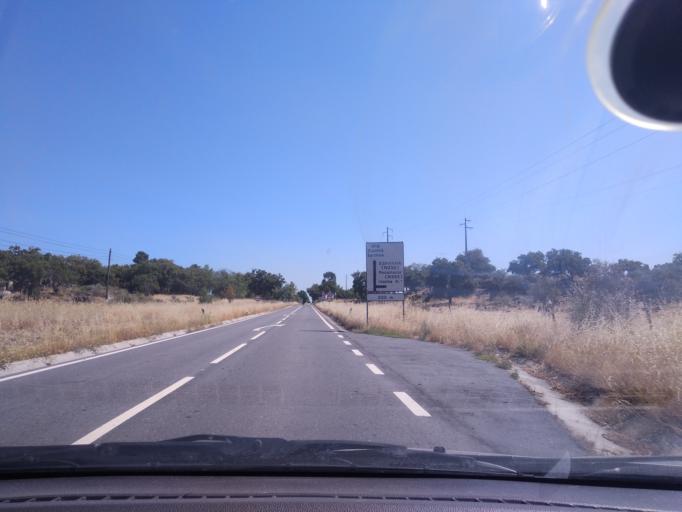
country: PT
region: Guarda
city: Alcains
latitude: 39.9221
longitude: -7.4680
